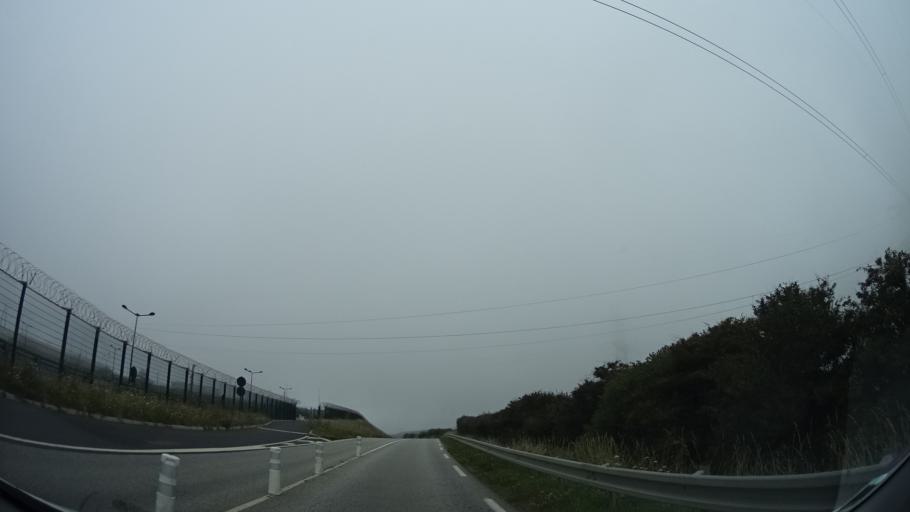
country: FR
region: Lower Normandy
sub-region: Departement de la Manche
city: Flamanville
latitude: 49.5355
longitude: -1.8768
